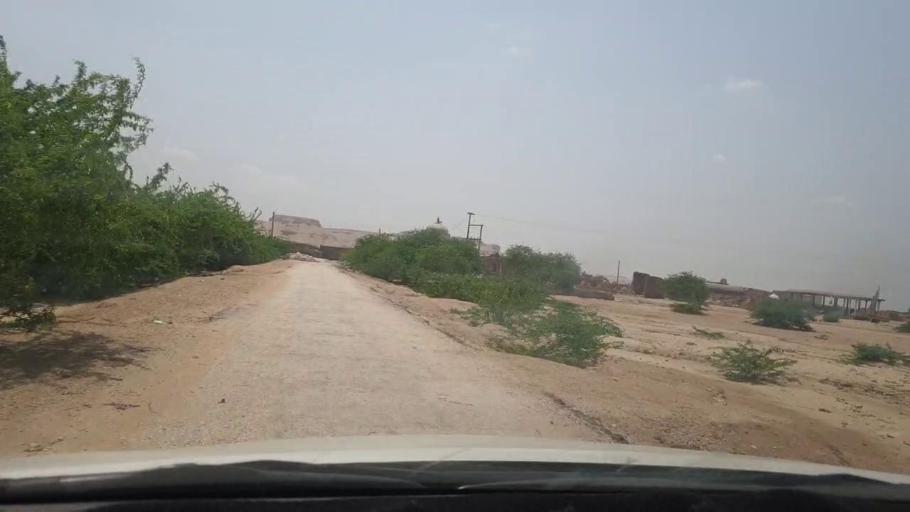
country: PK
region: Sindh
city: Khairpur
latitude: 27.5289
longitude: 68.9043
